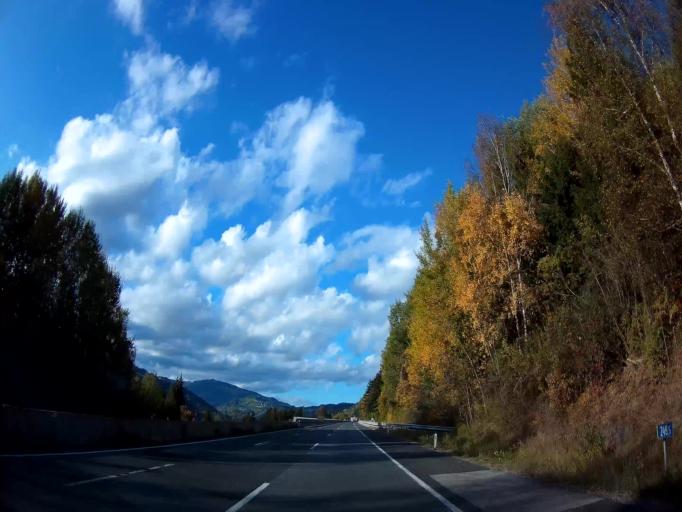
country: AT
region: Carinthia
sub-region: Politischer Bezirk Wolfsberg
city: Wolfsberg
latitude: 46.8720
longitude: 14.8345
